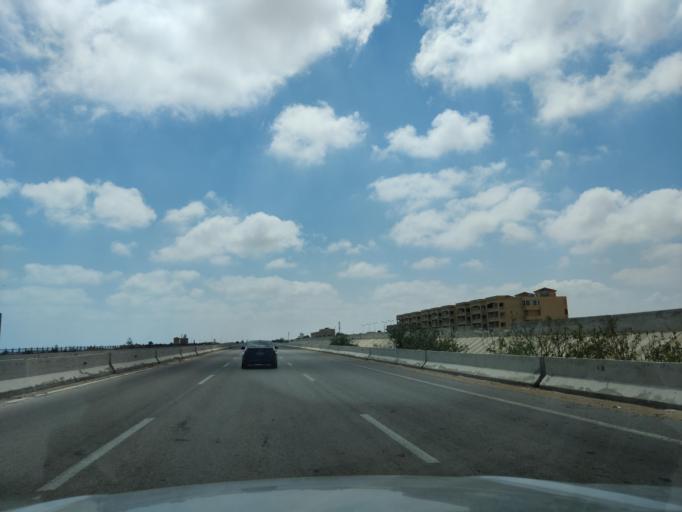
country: EG
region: Muhafazat Matruh
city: Al `Alamayn
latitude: 30.8211
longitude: 29.0113
